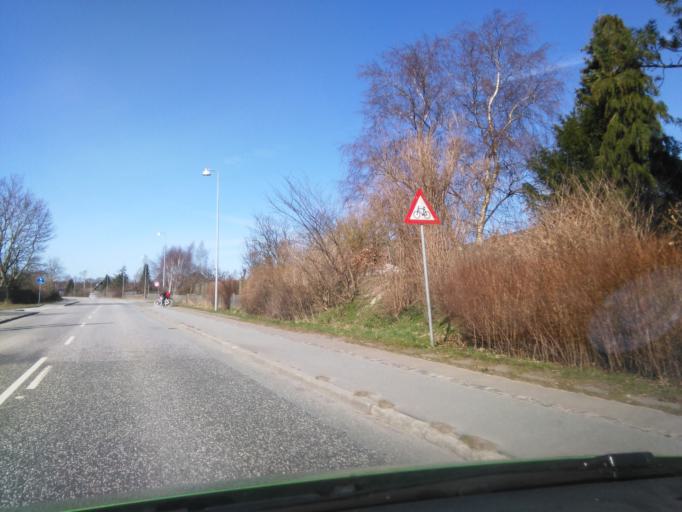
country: DK
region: Central Jutland
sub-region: Favrskov Kommune
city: Hinnerup
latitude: 56.2548
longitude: 10.0674
